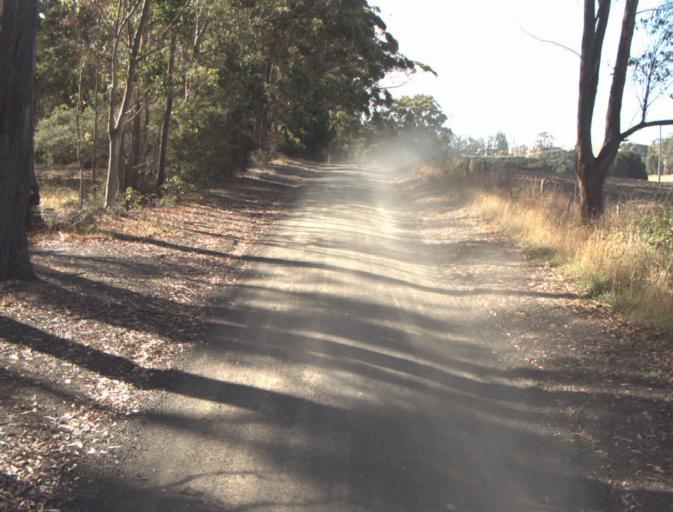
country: AU
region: Tasmania
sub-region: Dorset
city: Bridport
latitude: -41.1580
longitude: 147.2359
